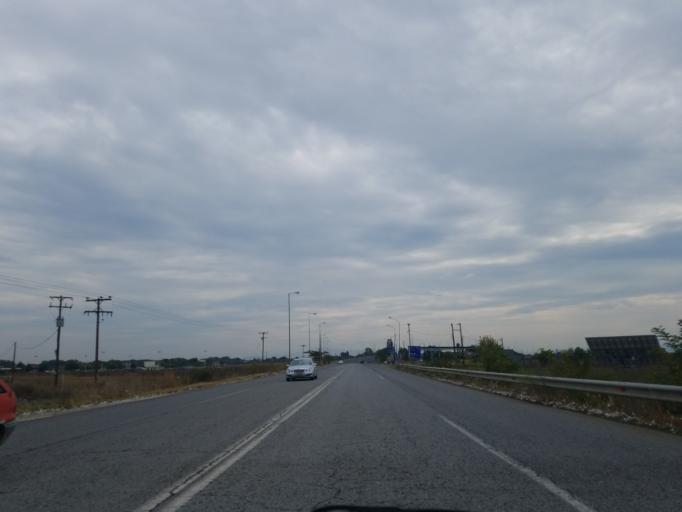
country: GR
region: Thessaly
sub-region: Nomos Kardhitsas
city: Sofades
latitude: 39.3456
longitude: 22.0761
